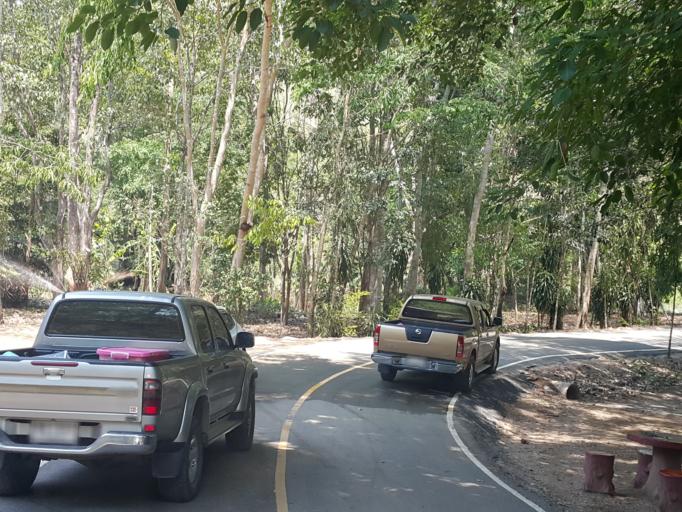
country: TH
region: Kanchanaburi
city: Sai Yok
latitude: 14.1875
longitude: 98.9592
